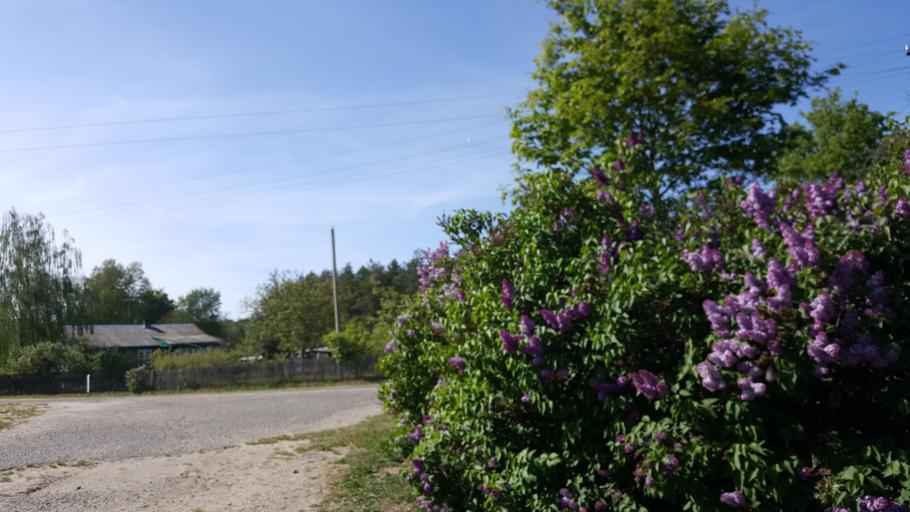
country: BY
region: Brest
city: Zhabinka
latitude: 52.3156
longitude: 24.0016
